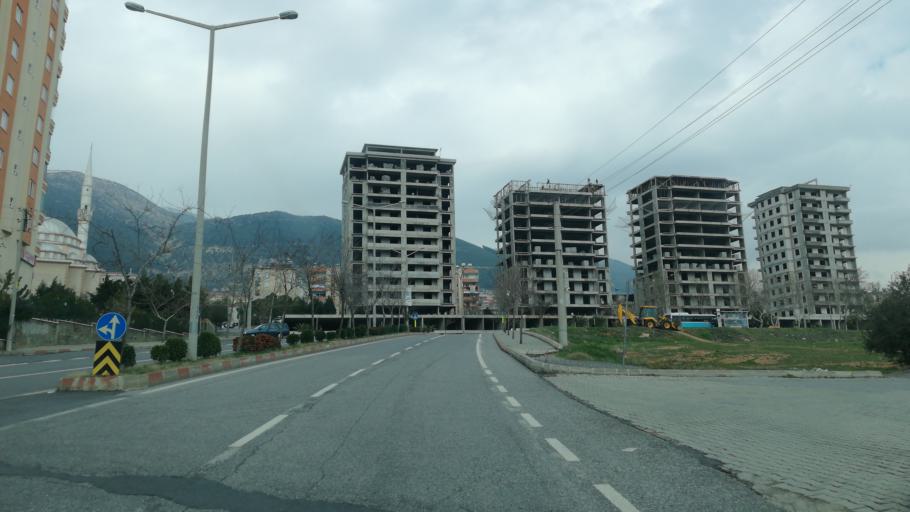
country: TR
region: Kahramanmaras
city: Kahramanmaras
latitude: 37.5916
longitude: 36.8637
